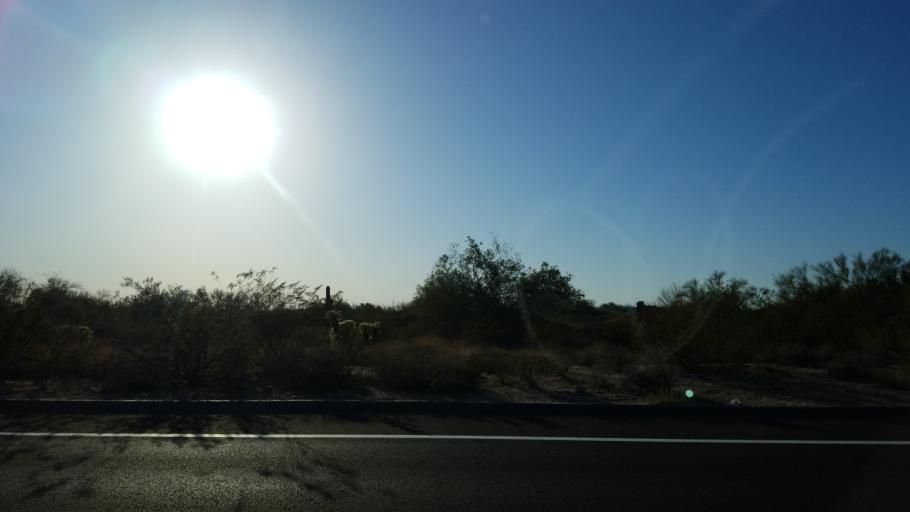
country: US
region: Arizona
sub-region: Maricopa County
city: Paradise Valley
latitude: 33.6703
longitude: -111.8907
